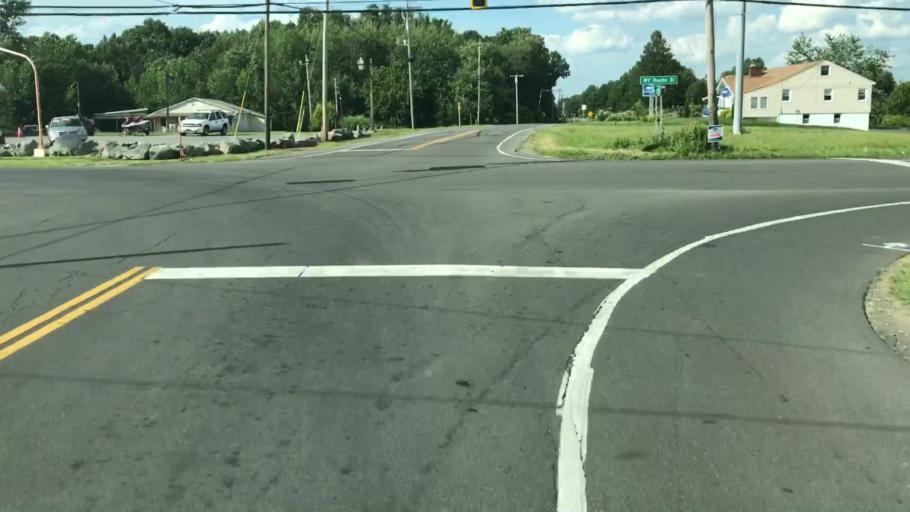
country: US
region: New York
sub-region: Onondaga County
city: Brewerton
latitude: 43.1865
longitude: -76.1999
